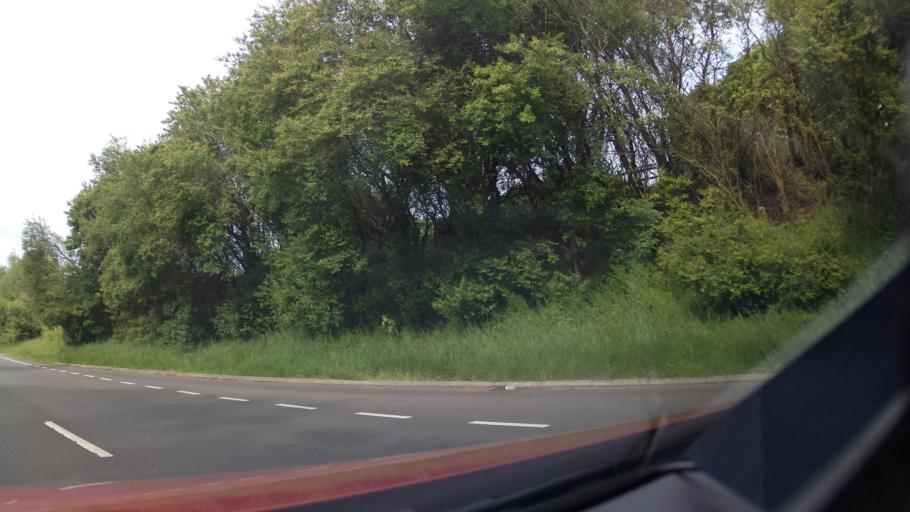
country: GB
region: England
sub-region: Northumberland
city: Berwick-Upon-Tweed
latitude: 55.7638
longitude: -2.0440
